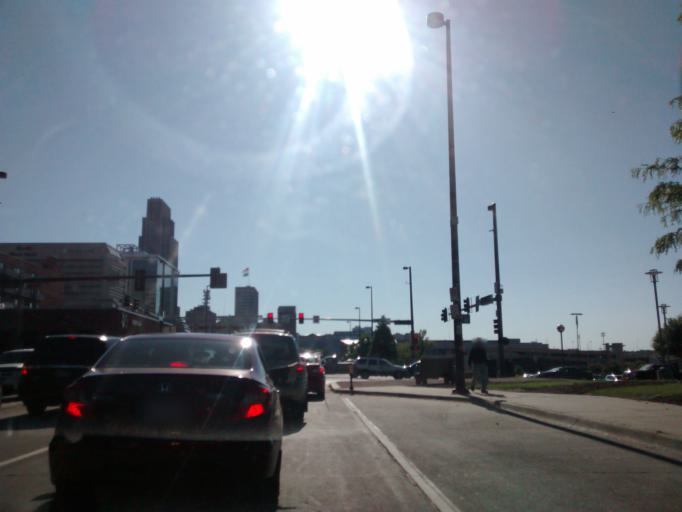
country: US
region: Nebraska
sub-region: Douglas County
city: Omaha
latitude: 41.2607
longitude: -95.9286
